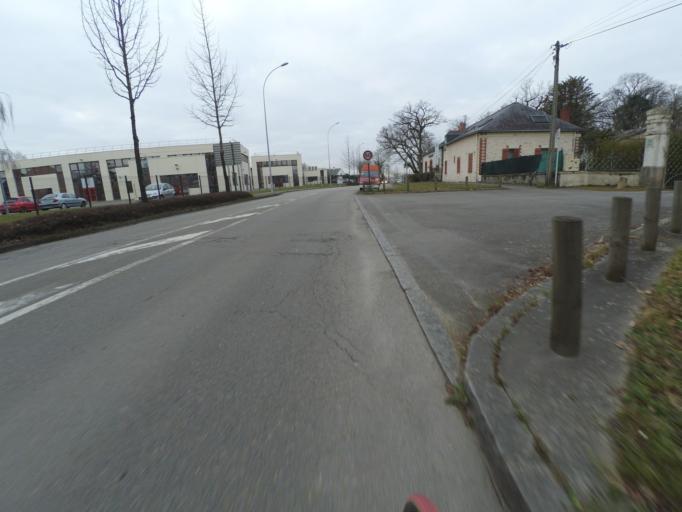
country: FR
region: Pays de la Loire
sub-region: Departement de la Loire-Atlantique
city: Sainte-Luce-sur-Loire
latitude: 47.2693
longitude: -1.4866
